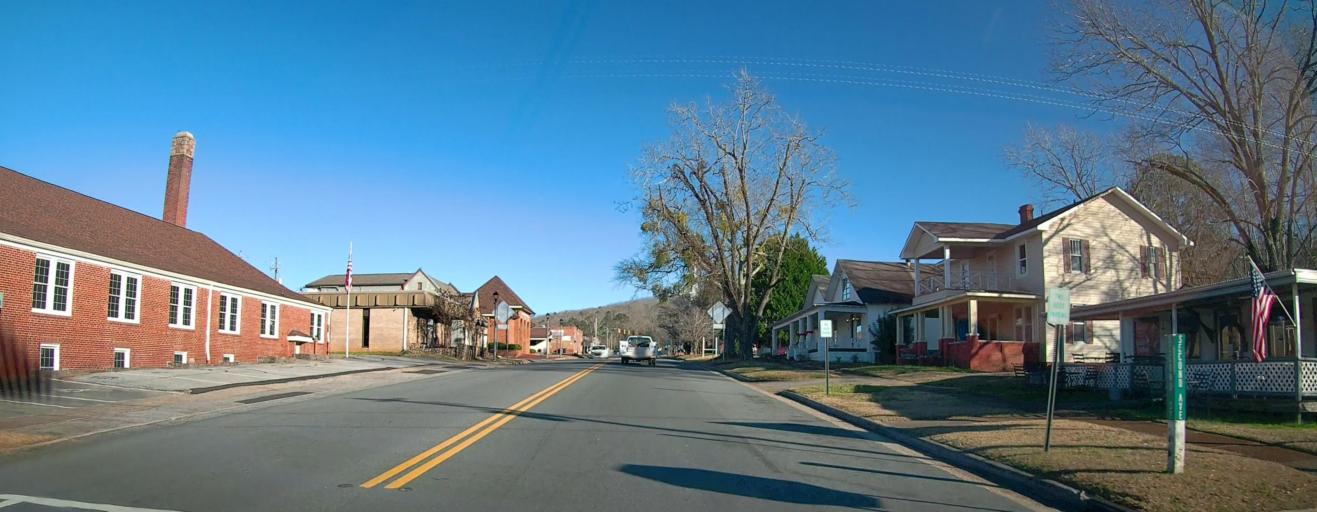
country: US
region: Georgia
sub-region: Meriwether County
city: Manchester
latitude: 32.8518
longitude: -84.6153
